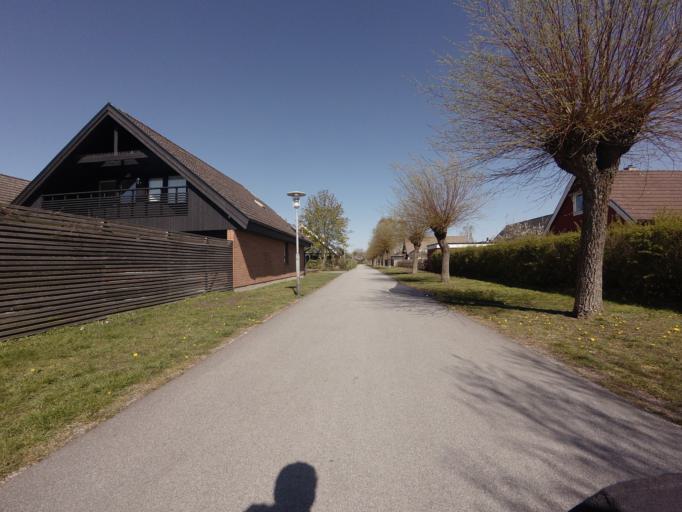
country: SE
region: Skane
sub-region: Kavlinge Kommun
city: Loddekopinge
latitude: 55.7631
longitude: 13.0052
